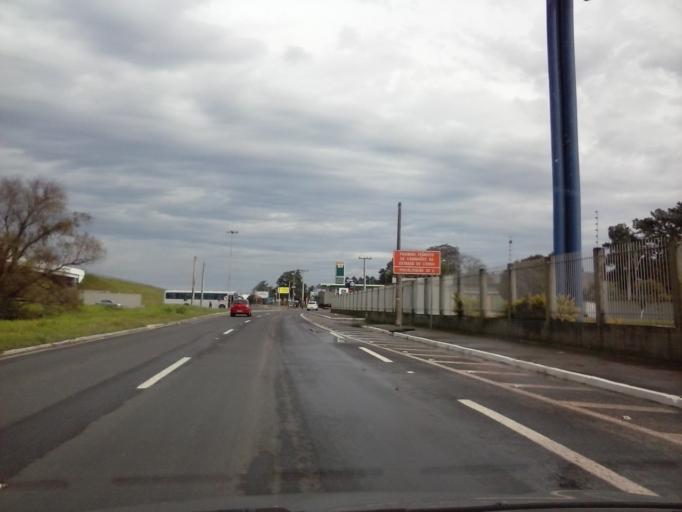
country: BR
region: Rio Grande do Sul
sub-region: Porto Alegre
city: Porto Alegre
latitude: -30.0016
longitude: -51.3055
